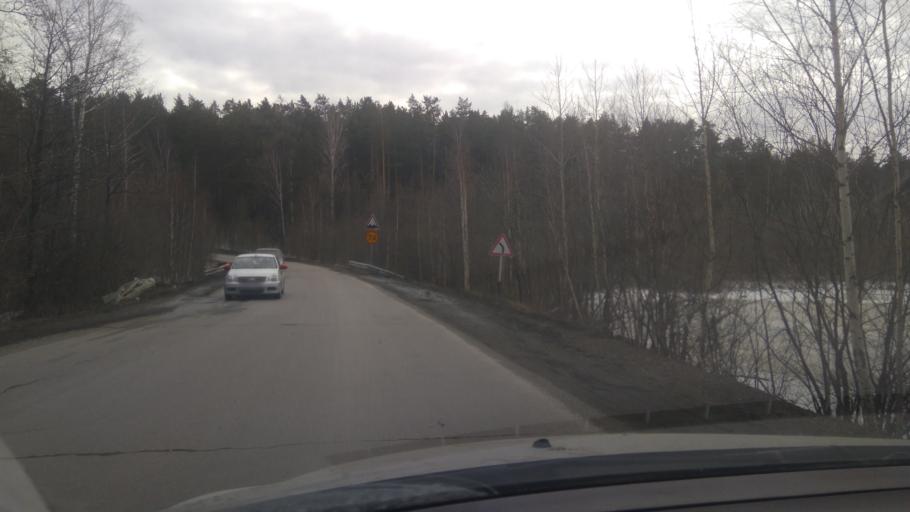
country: RU
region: Sverdlovsk
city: Severka
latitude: 56.8360
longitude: 60.3822
